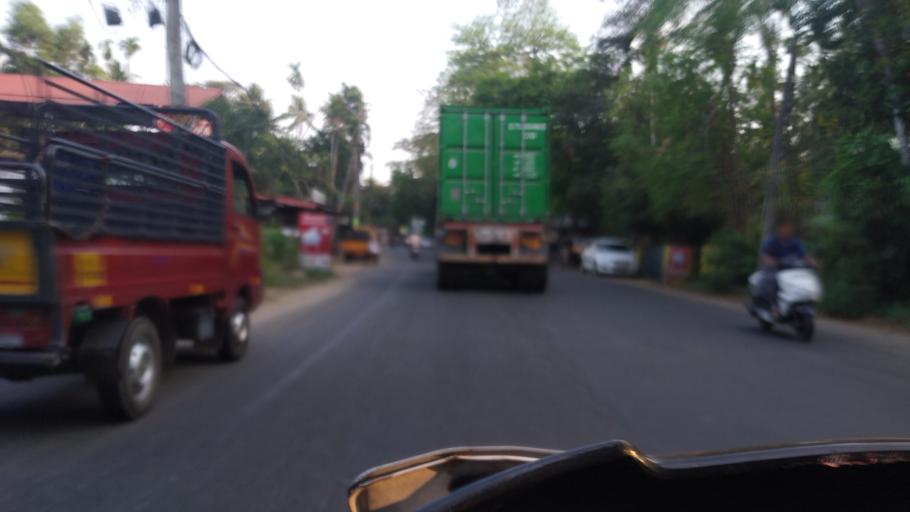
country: IN
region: Kerala
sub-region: Thrissur District
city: Irinjalakuda
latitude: 10.3391
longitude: 76.1376
